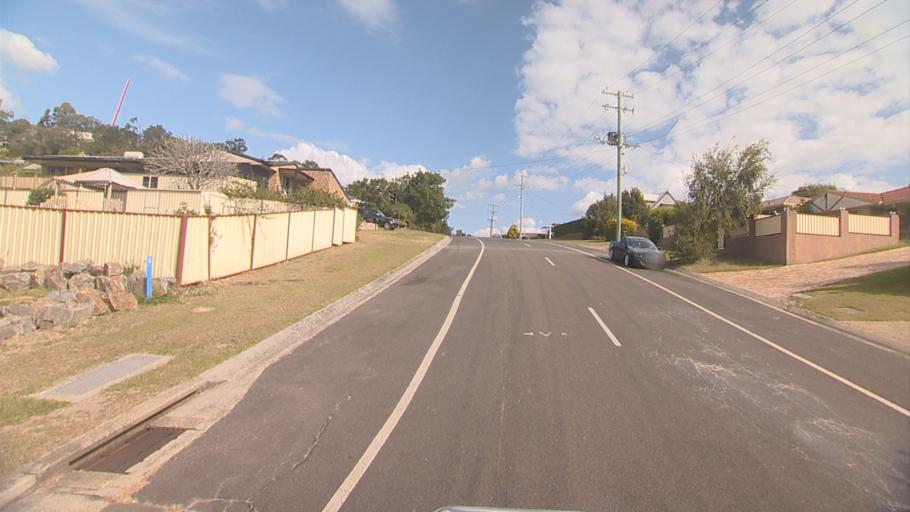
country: AU
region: Queensland
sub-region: Logan
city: Windaroo
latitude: -27.7248
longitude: 153.1974
